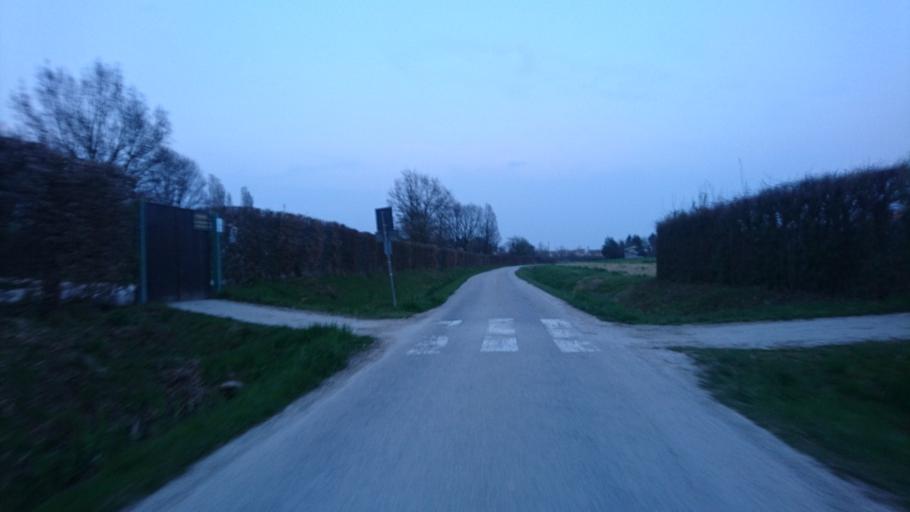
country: IT
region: Veneto
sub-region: Provincia di Padova
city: Saccolongo
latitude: 45.3862
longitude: 11.7541
